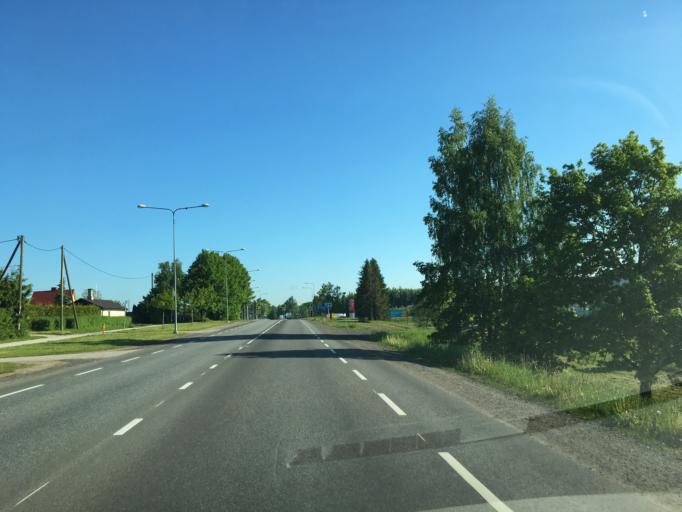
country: EE
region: Tartu
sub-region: Tartu linn
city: Tartu
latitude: 58.4048
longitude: 26.7084
